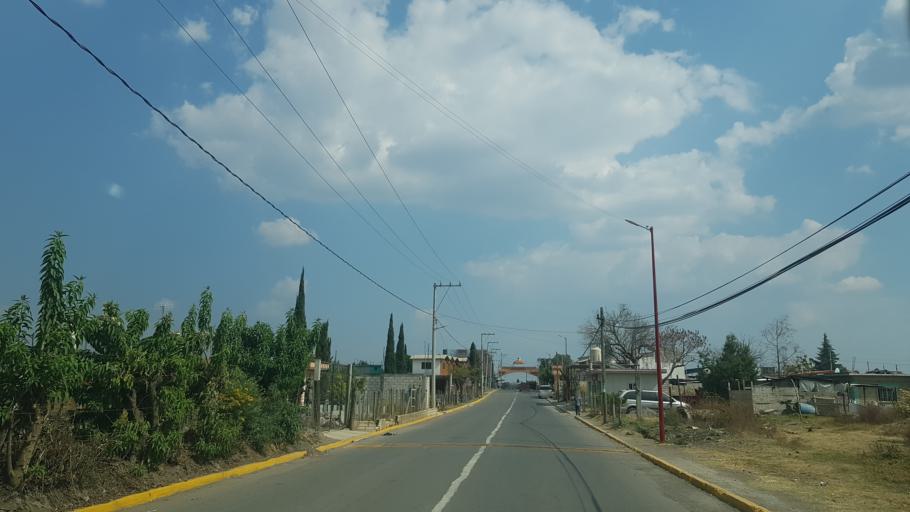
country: MX
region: Puebla
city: San Juan Amecac
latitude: 18.8290
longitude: -98.6572
